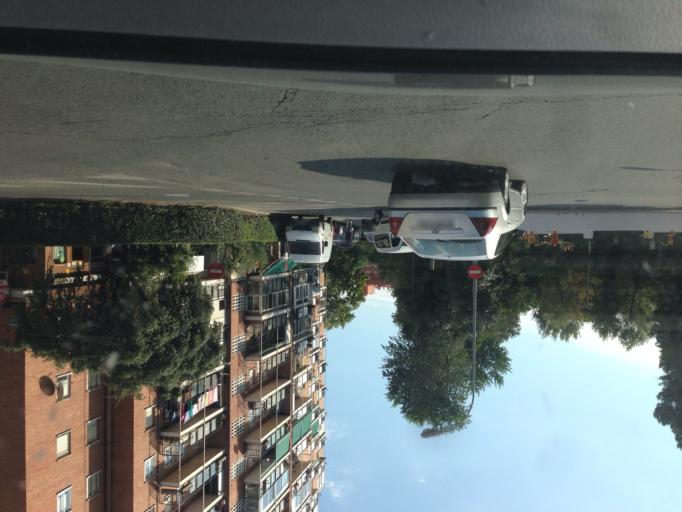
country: ES
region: Madrid
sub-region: Provincia de Madrid
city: Alcala de Henares
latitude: 40.4900
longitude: -3.3759
